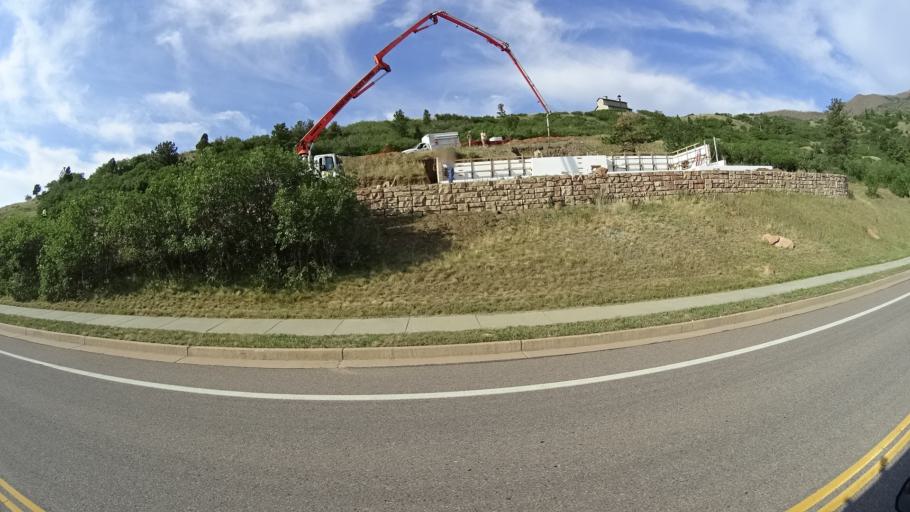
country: US
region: Colorado
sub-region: El Paso County
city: Air Force Academy
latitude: 38.9440
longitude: -104.8778
